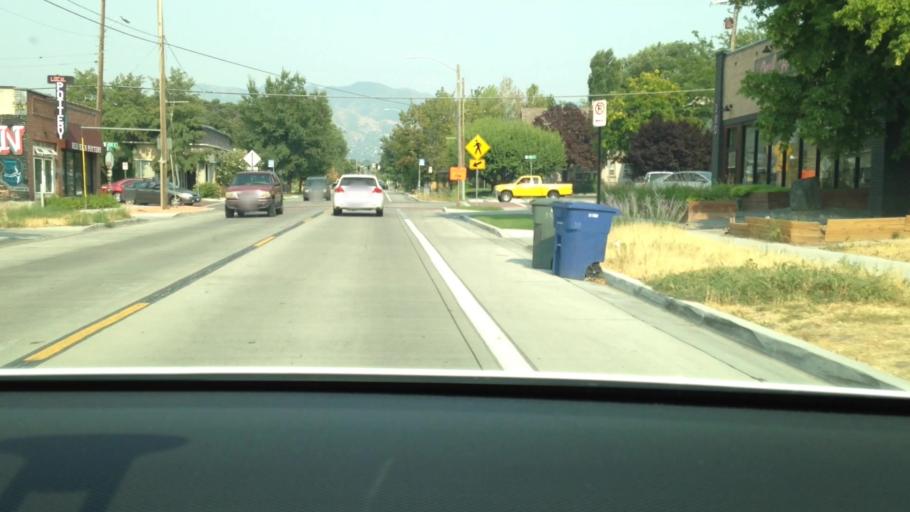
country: US
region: Utah
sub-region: Salt Lake County
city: South Salt Lake
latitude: 40.7335
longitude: -111.8804
